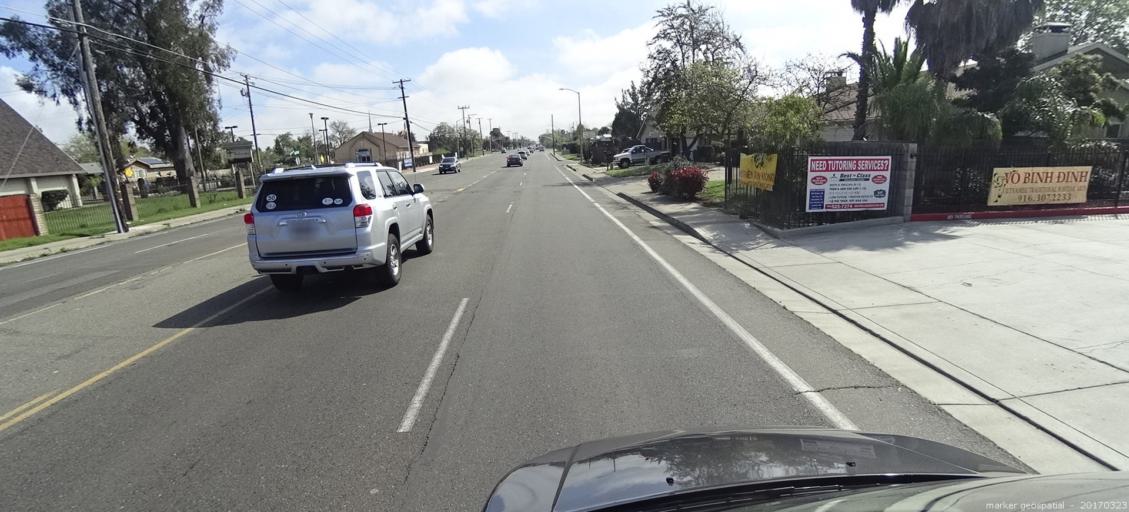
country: US
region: California
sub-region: Sacramento County
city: Florin
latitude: 38.5104
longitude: -121.4306
